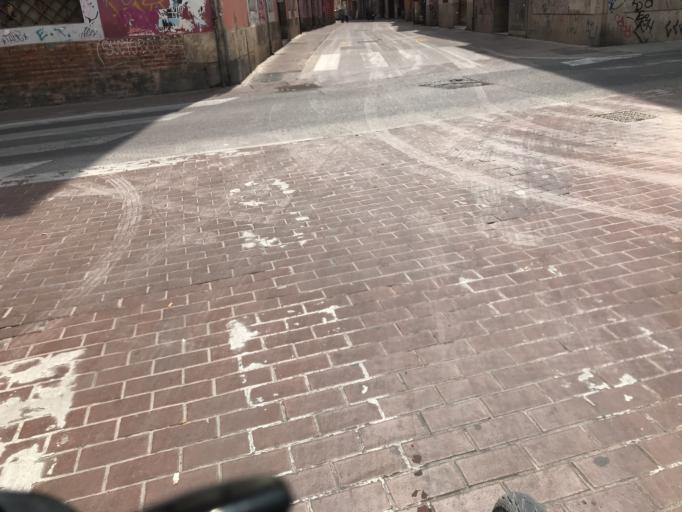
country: ES
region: Valencia
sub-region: Provincia de Valencia
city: Valencia
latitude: 39.4753
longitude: -0.3808
